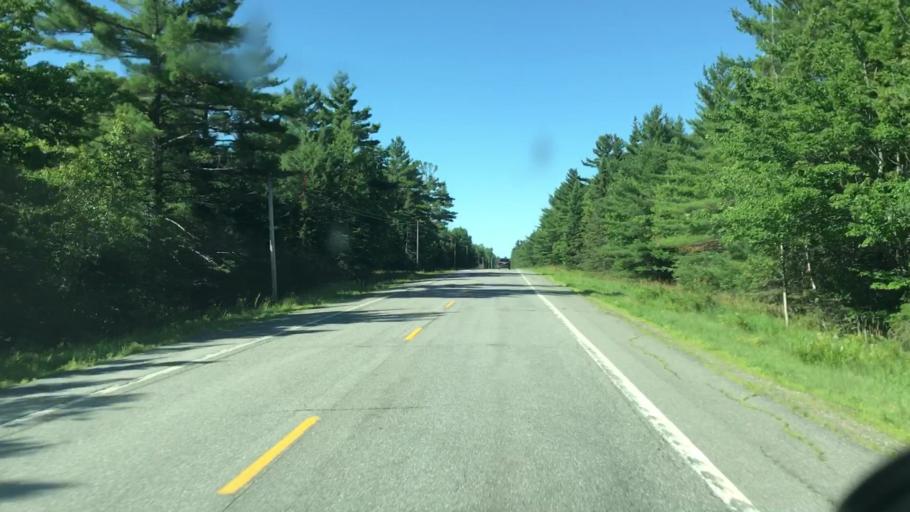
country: US
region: Maine
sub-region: Penobscot County
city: Enfield
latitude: 45.3078
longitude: -68.6105
